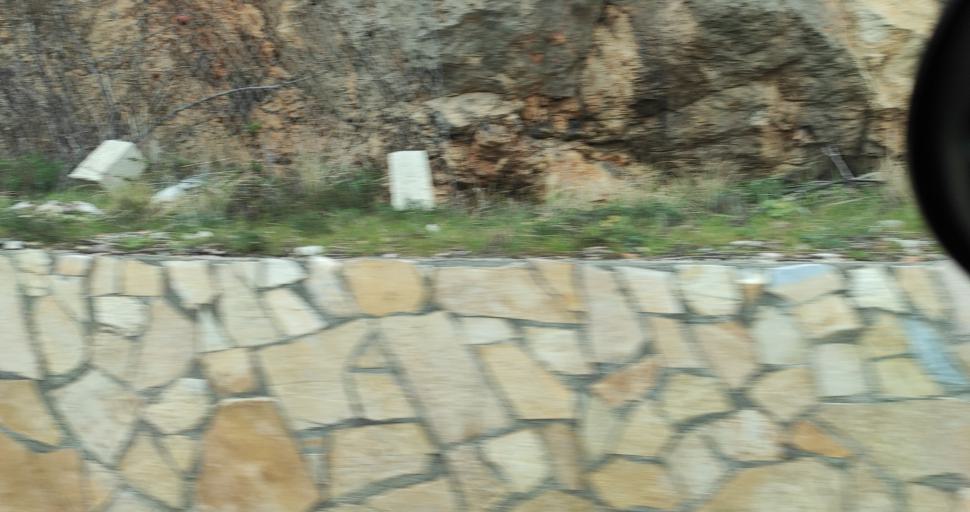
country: AL
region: Lezhe
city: Shengjin
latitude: 41.8028
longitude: 19.6150
